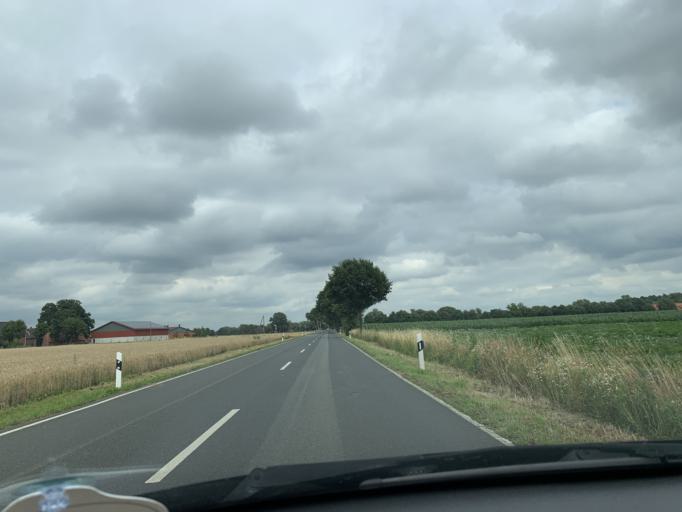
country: DE
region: North Rhine-Westphalia
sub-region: Regierungsbezirk Munster
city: Wadersloh
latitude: 51.7128
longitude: 8.3015
